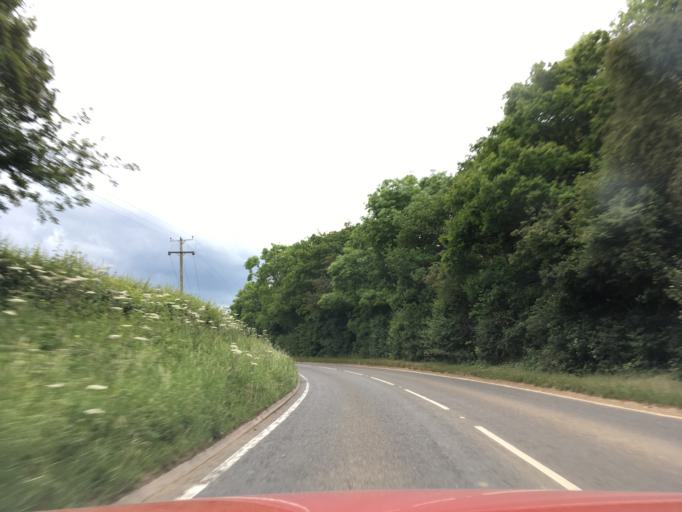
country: GB
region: England
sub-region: Central Bedfordshire
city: Potsgrove
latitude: 51.9567
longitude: -0.6444
